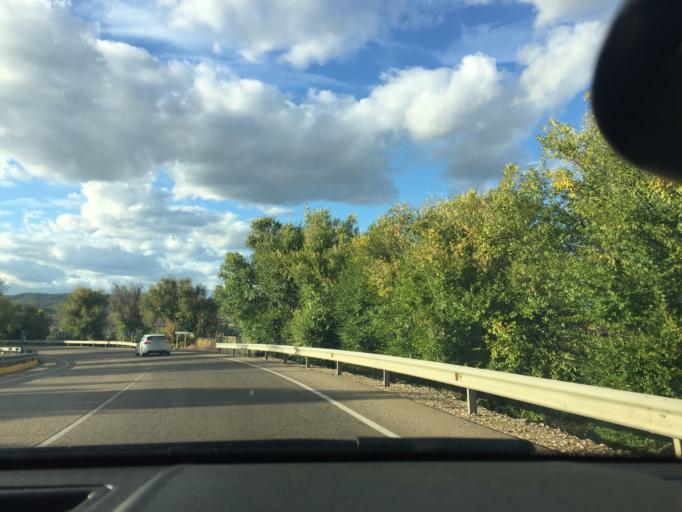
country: ES
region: Andalusia
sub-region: Province of Cordoba
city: El Carpio
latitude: 37.9527
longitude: -4.5127
